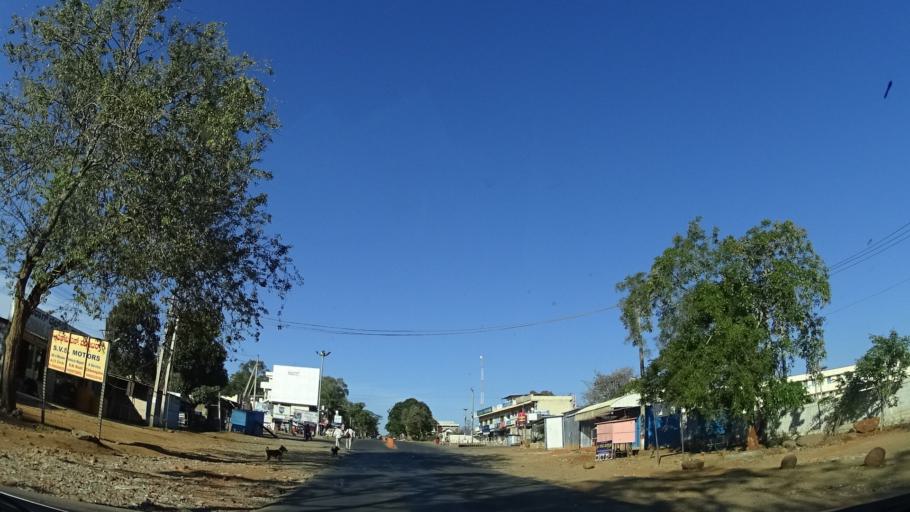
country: IN
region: Karnataka
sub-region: Chikmagalur
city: Chikmagalur
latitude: 13.3343
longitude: 75.7975
